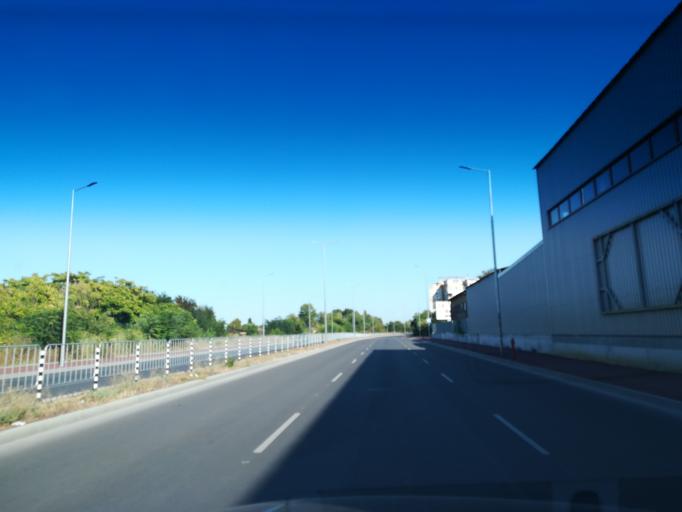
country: BG
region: Plovdiv
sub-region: Obshtina Plovdiv
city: Plovdiv
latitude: 42.1645
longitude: 24.7602
